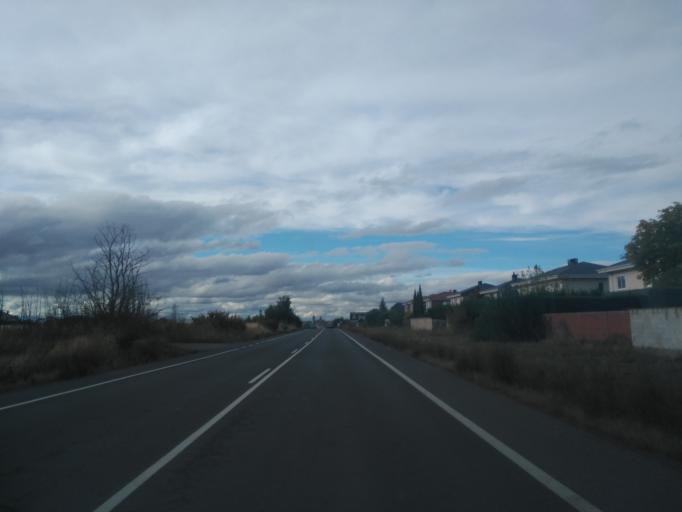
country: ES
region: Castille and Leon
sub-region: Provincia de Salamanca
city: Santa Marta de Tormes
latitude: 40.9358
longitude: -5.6297
